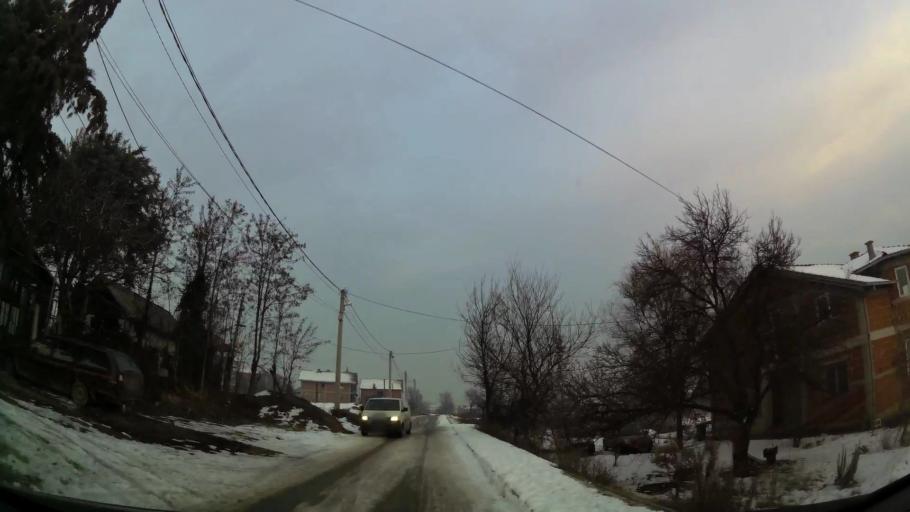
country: MK
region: Suto Orizari
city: Suto Orizare
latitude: 42.0394
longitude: 21.4057
